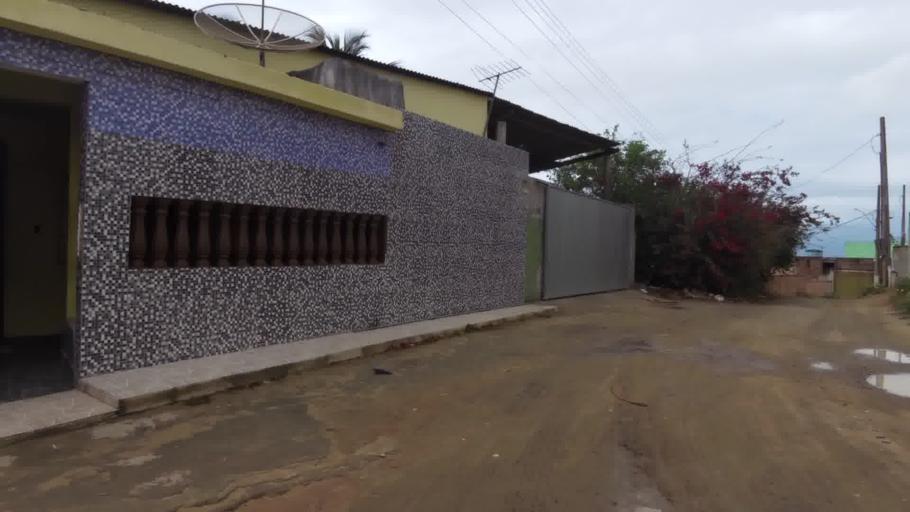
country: BR
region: Espirito Santo
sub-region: Marataizes
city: Marataizes
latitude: -21.0289
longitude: -40.8201
